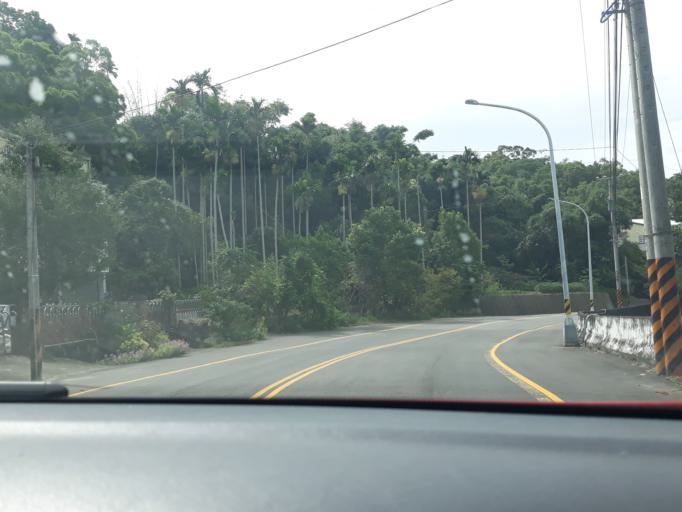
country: TW
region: Taiwan
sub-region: Miaoli
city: Miaoli
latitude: 24.5518
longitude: 120.8048
